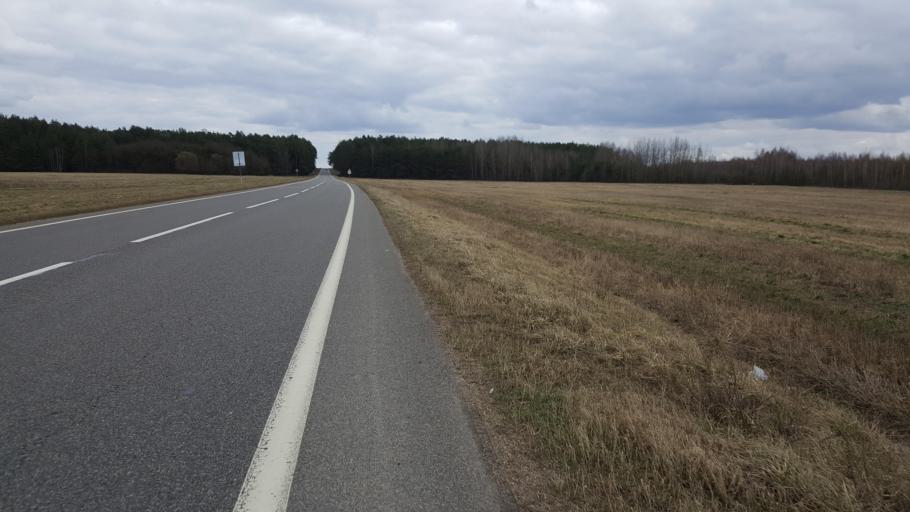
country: BY
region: Brest
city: Kamyanyuki
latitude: 52.4809
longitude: 23.8027
